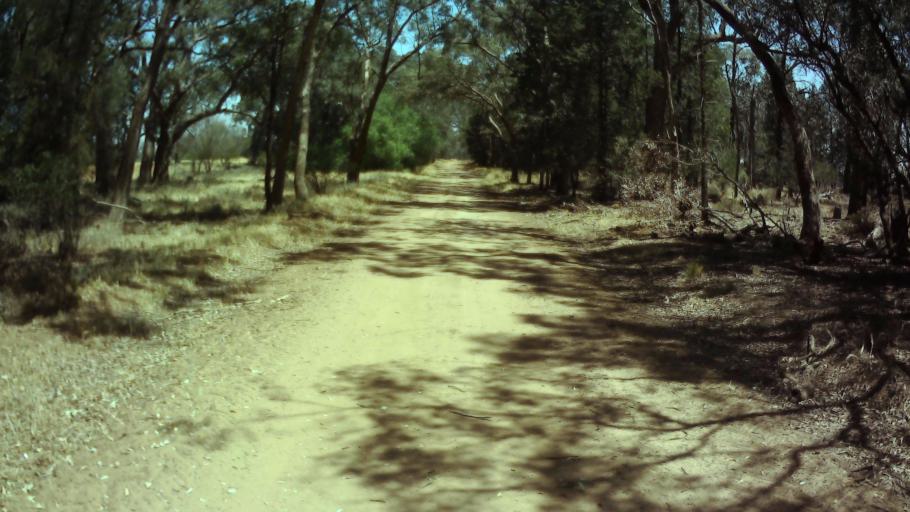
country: AU
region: New South Wales
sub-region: Weddin
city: Grenfell
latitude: -34.0408
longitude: 147.8474
